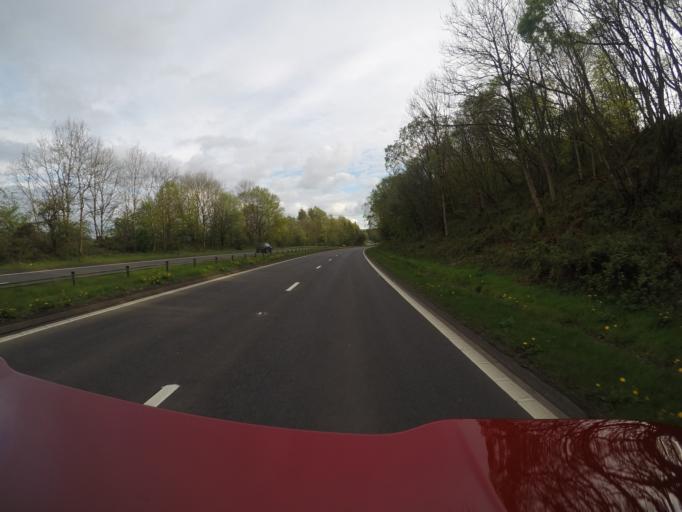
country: GB
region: Scotland
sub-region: West Dunbartonshire
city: Alexandria
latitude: 55.9831
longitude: -4.5871
